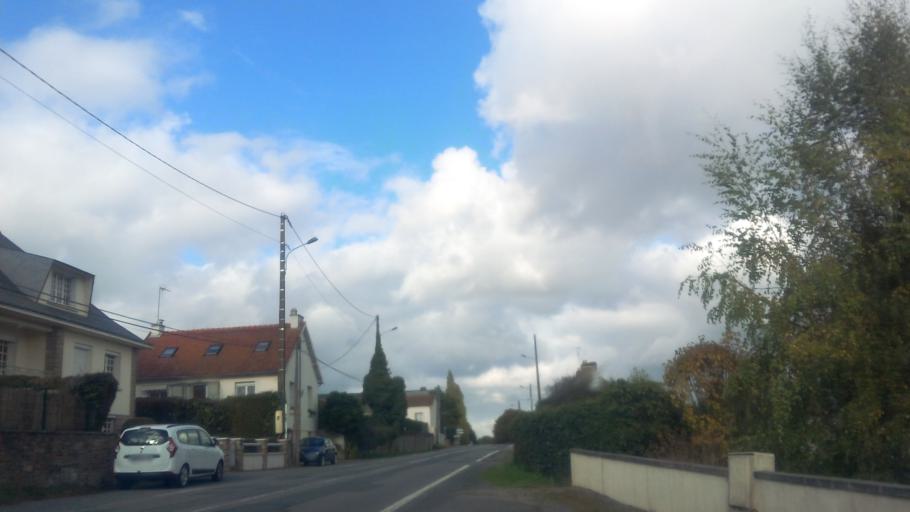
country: FR
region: Brittany
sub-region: Departement d'Ille-et-Vilaine
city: Redon
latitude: 47.6650
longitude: -2.0820
